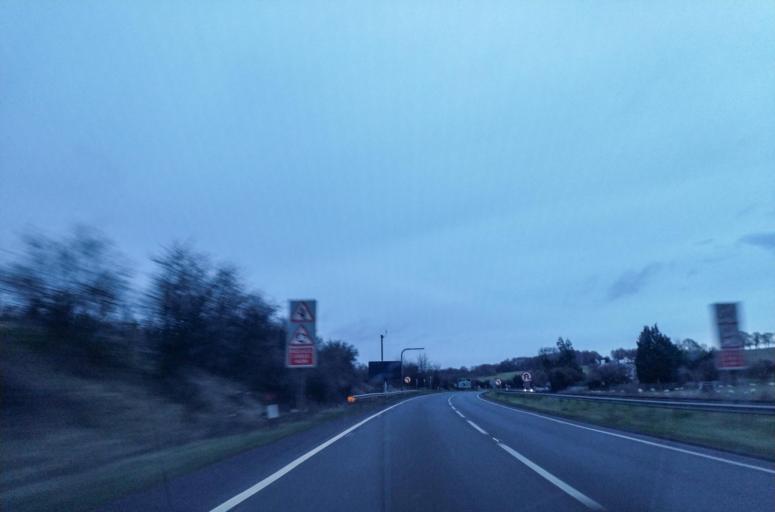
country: GB
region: England
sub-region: Kent
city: Newington
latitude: 51.3233
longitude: 0.6529
